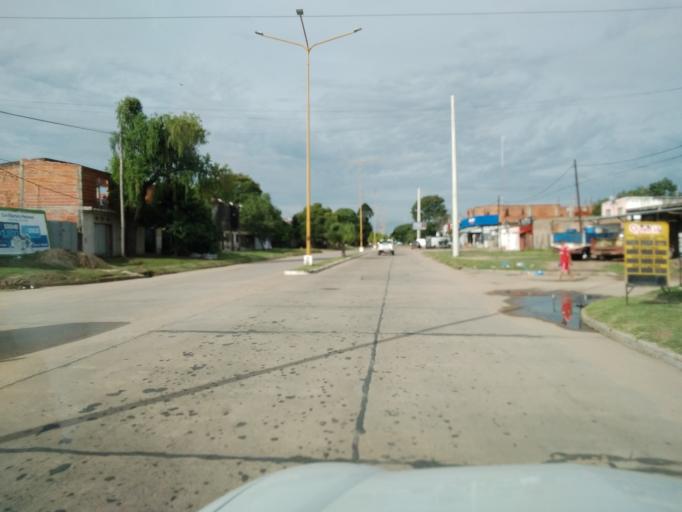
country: AR
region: Corrientes
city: Corrientes
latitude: -27.4610
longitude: -58.7804
